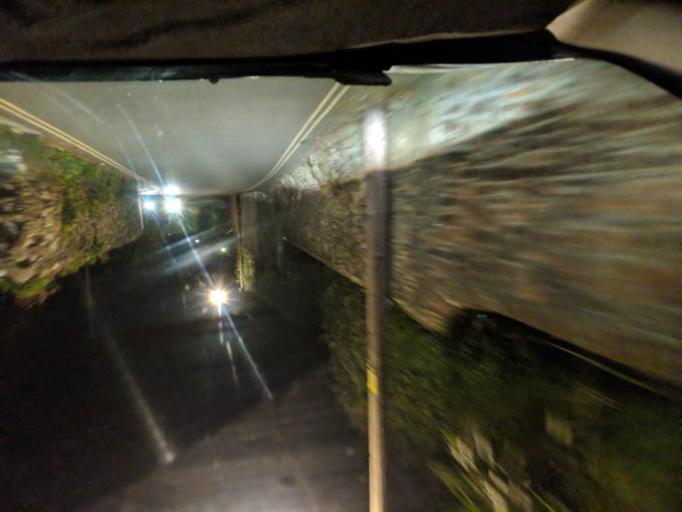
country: GB
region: England
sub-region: Cornwall
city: Mevagissey
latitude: 50.2701
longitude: -4.7895
